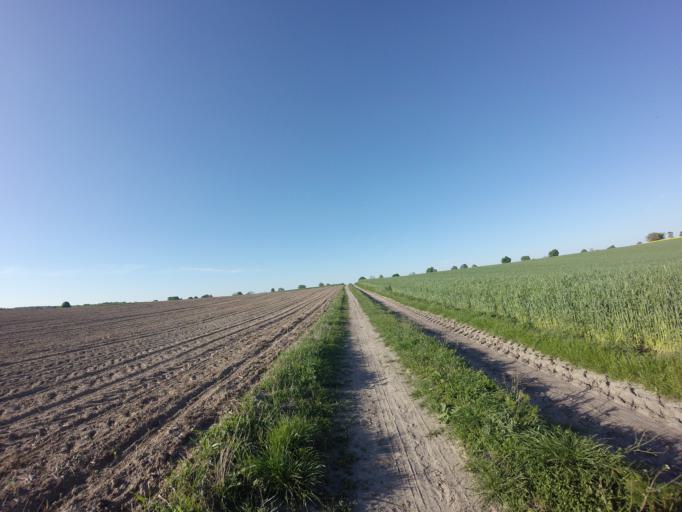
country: PL
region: West Pomeranian Voivodeship
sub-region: Powiat choszczenski
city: Choszczno
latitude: 53.1313
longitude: 15.3606
